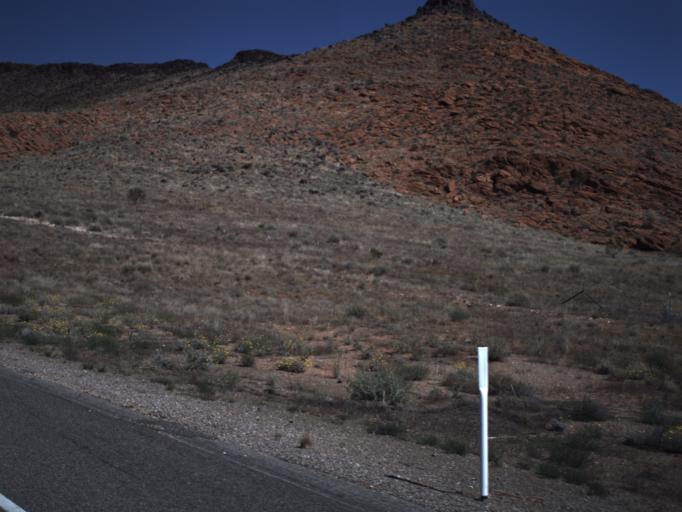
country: US
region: Utah
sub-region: Washington County
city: Saint George
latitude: 37.1569
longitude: -113.6029
